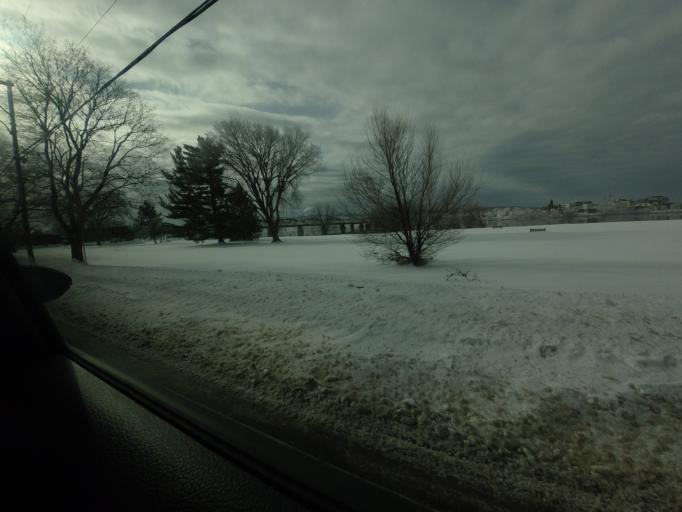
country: CA
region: New Brunswick
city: Fredericton
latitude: 45.9607
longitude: -66.6247
